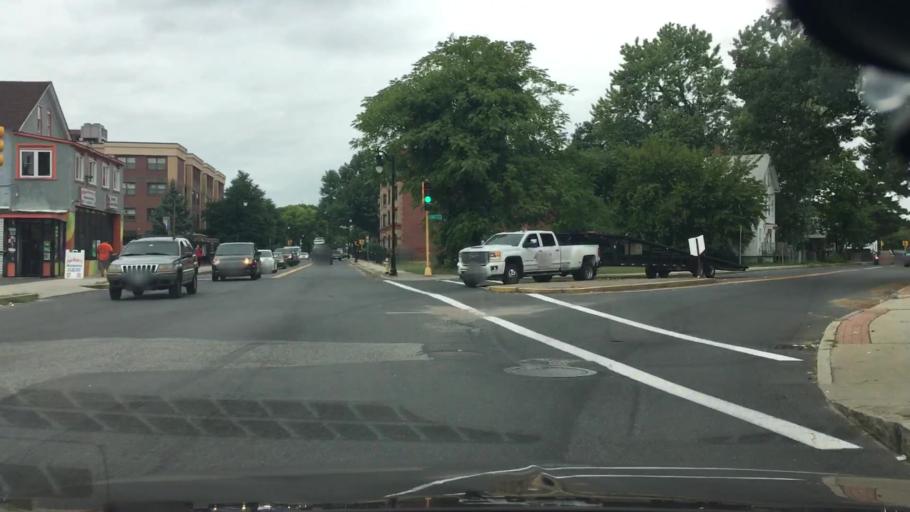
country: US
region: Massachusetts
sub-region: Hampden County
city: Springfield
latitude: 42.1055
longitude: -72.5733
